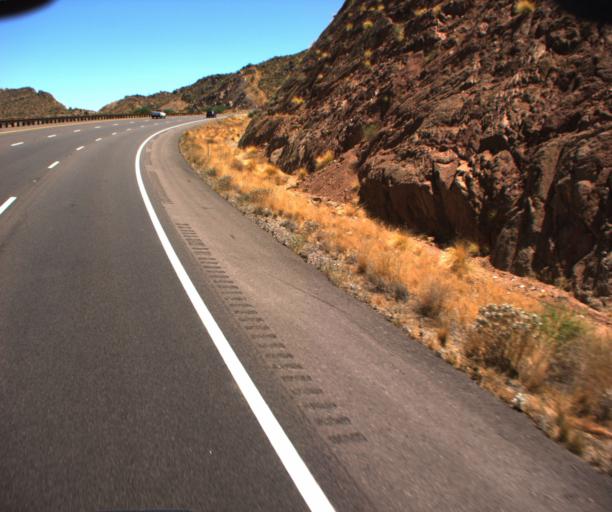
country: US
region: Arizona
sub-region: Maricopa County
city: Rio Verde
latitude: 33.7088
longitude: -111.5063
